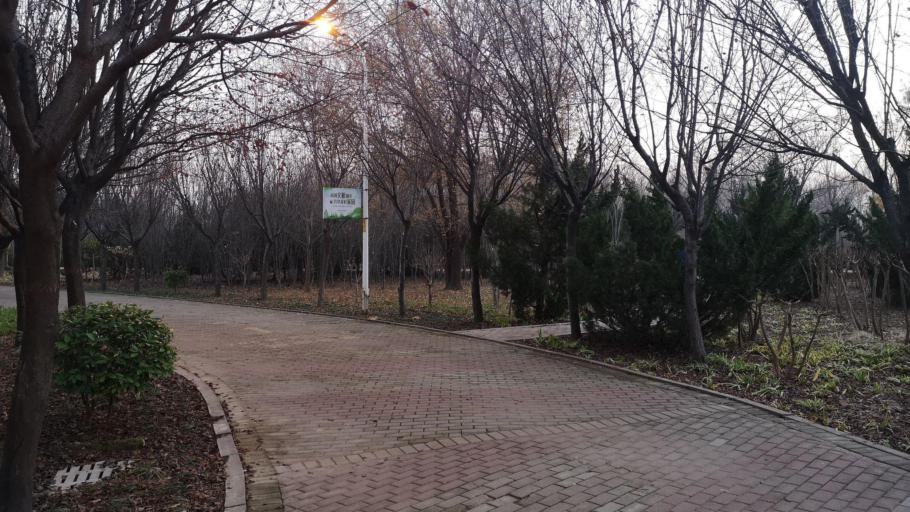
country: CN
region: Henan Sheng
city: Zhongyuanlu
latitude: 35.7427
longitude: 115.0609
